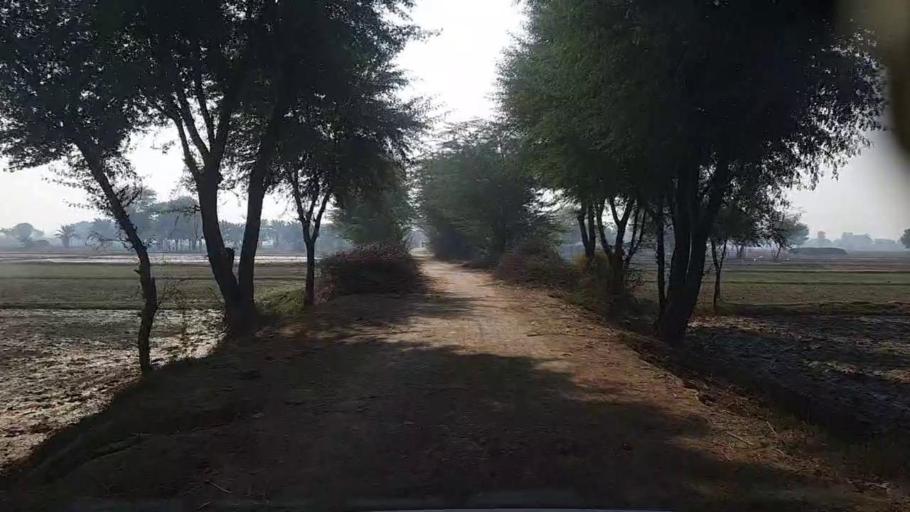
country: PK
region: Sindh
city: Kandiari
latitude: 26.9774
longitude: 68.4694
